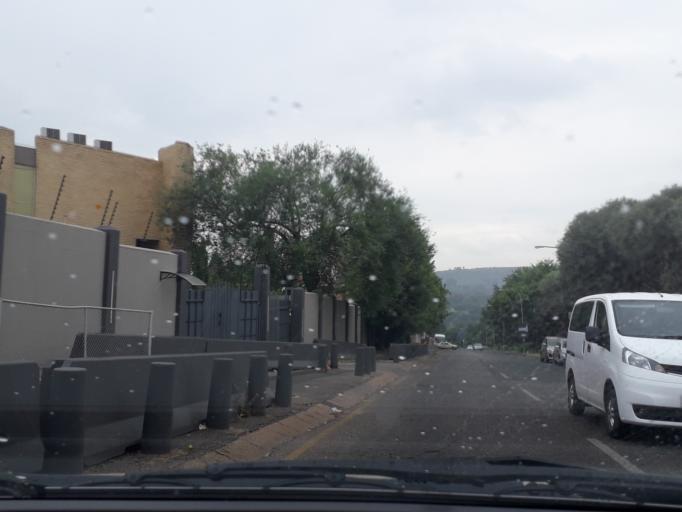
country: ZA
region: Gauteng
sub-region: City of Johannesburg Metropolitan Municipality
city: Modderfontein
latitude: -26.1424
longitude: 28.1065
